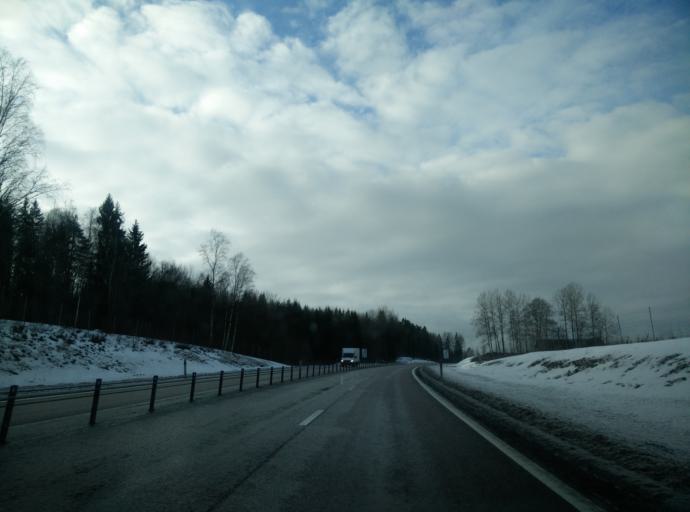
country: SE
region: Gaevleborg
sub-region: Sandvikens Kommun
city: Jarbo
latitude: 60.5723
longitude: 16.5309
